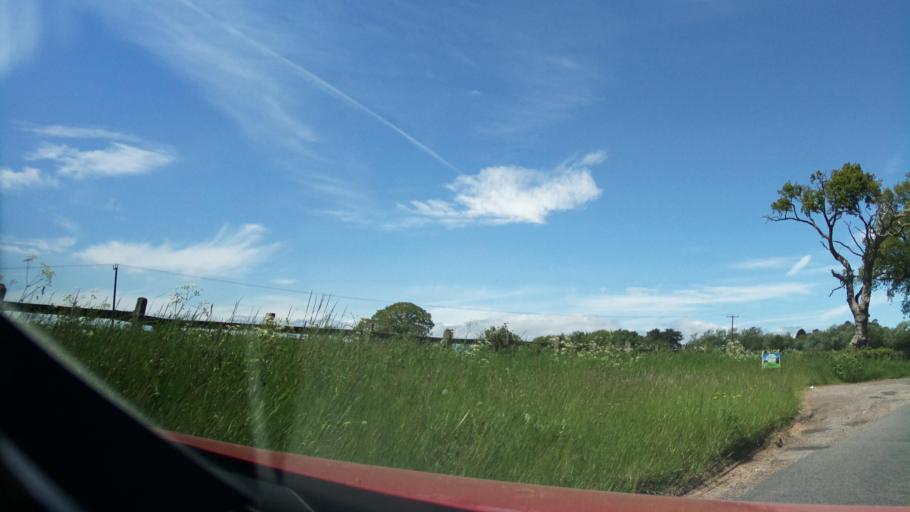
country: GB
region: Wales
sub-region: Monmouthshire
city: Caldicot
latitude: 51.6331
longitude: -2.7455
